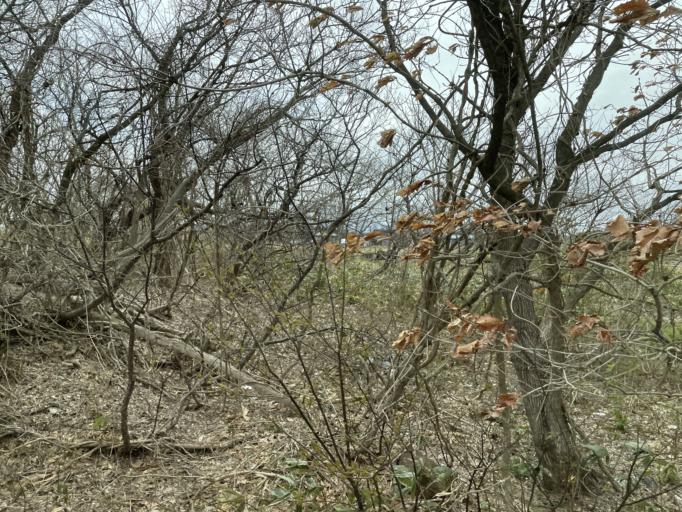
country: JP
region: Aomori
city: Shimokizukuri
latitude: 40.7863
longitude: 140.3078
